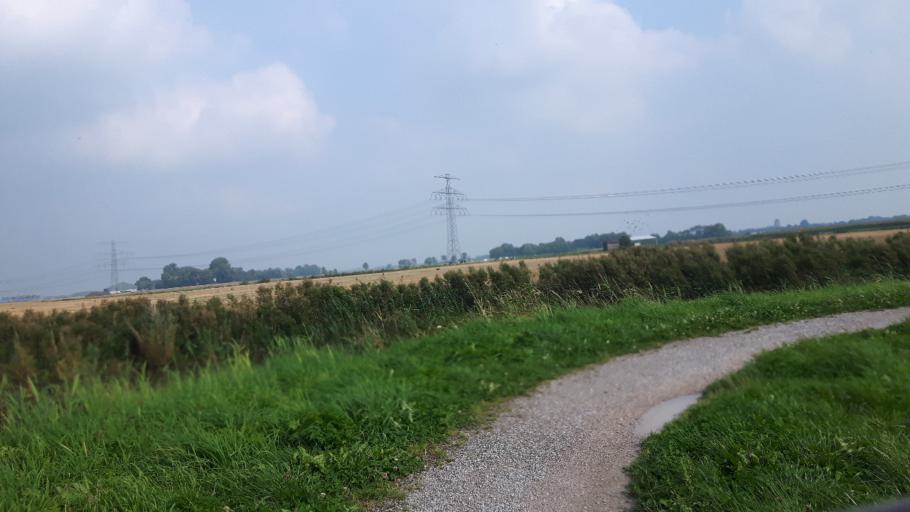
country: NL
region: Groningen
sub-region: Gemeente Bedum
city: Bedum
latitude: 53.3407
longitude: 6.7184
